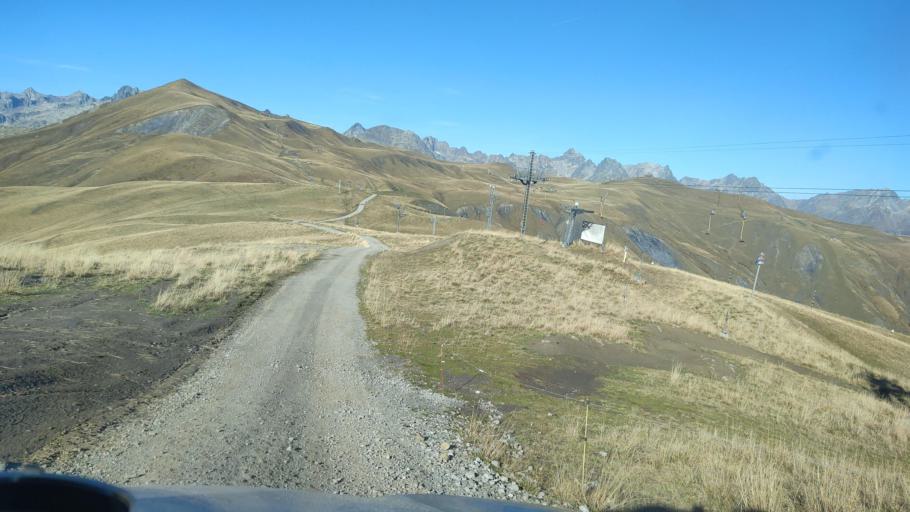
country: FR
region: Rhone-Alpes
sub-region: Departement de la Savoie
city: Saint-Jean-de-Maurienne
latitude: 45.2363
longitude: 6.2416
